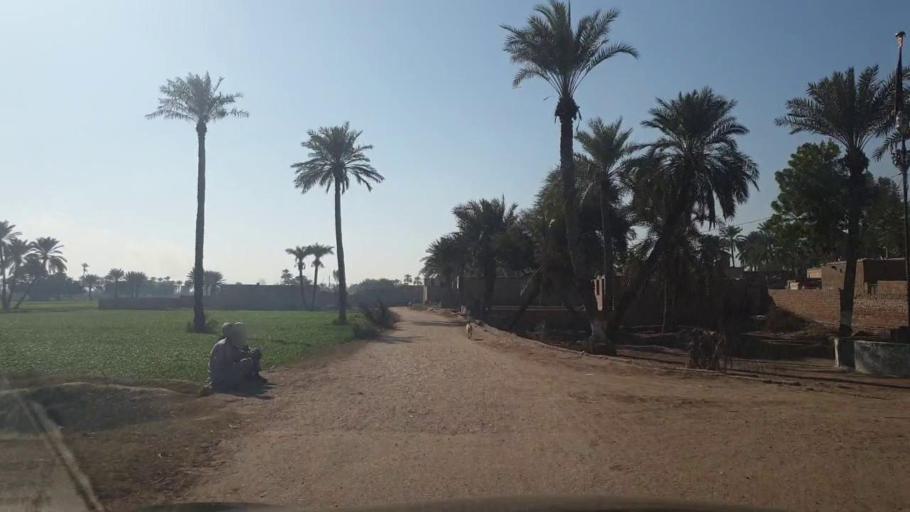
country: PK
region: Sindh
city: Ghotki
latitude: 27.9965
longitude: 69.3271
